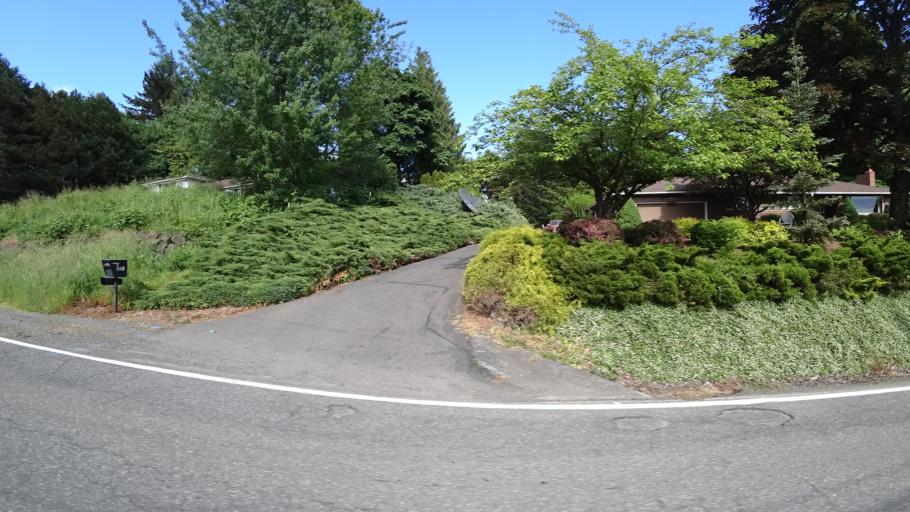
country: US
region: Oregon
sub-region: Washington County
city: Cedar Mill
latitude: 45.5717
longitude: -122.7902
